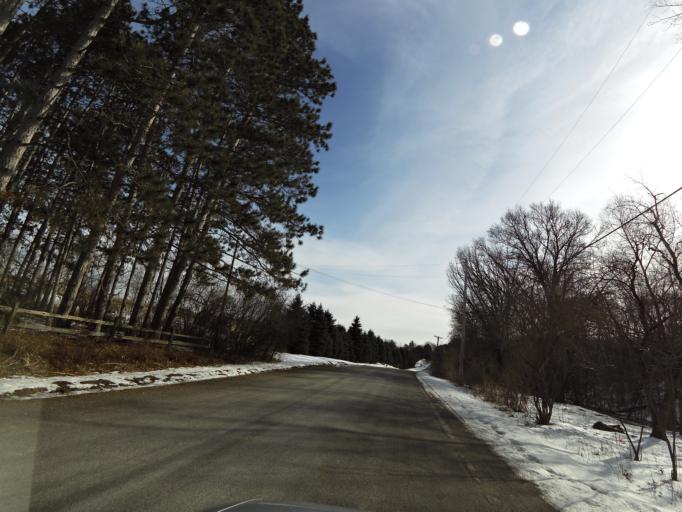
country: US
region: Minnesota
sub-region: Washington County
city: Afton
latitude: 44.9315
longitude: -92.8071
